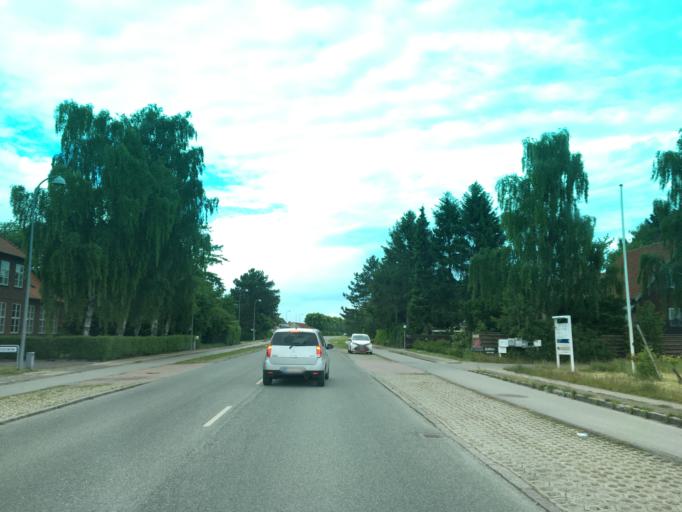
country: DK
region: Capital Region
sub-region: Hvidovre Kommune
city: Hvidovre
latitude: 55.6400
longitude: 12.4470
